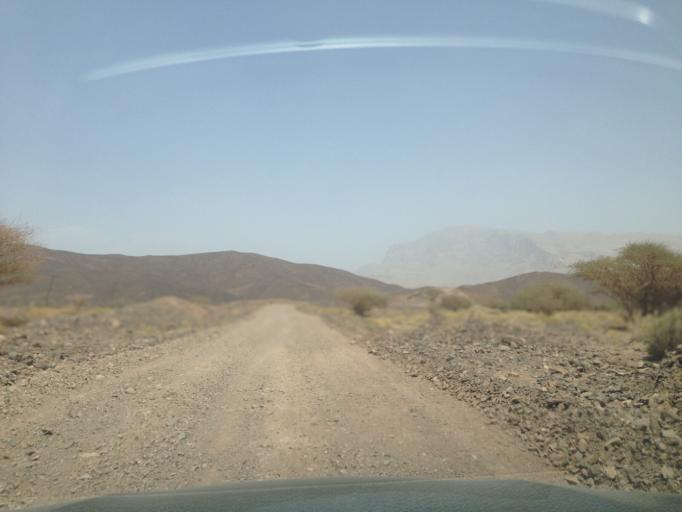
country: OM
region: Az Zahirah
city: `Ibri
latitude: 23.2008
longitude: 56.8698
